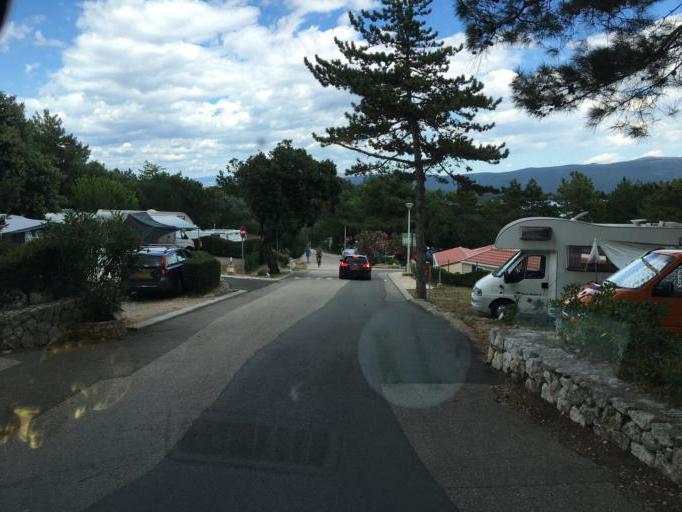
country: HR
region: Primorsko-Goranska
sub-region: Grad Krk
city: Krk
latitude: 45.0194
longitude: 14.5691
